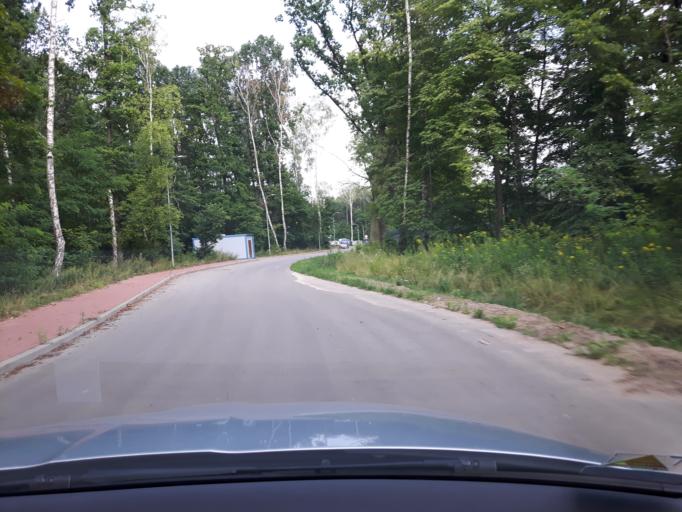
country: PL
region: Masovian Voivodeship
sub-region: Powiat wolominski
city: Zabki
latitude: 52.3019
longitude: 21.1104
